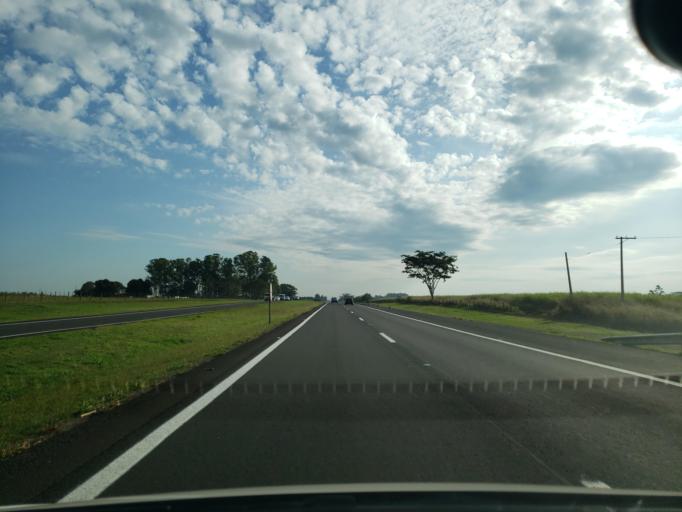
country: BR
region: Sao Paulo
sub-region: Guararapes
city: Guararapes
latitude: -21.2018
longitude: -50.5916
